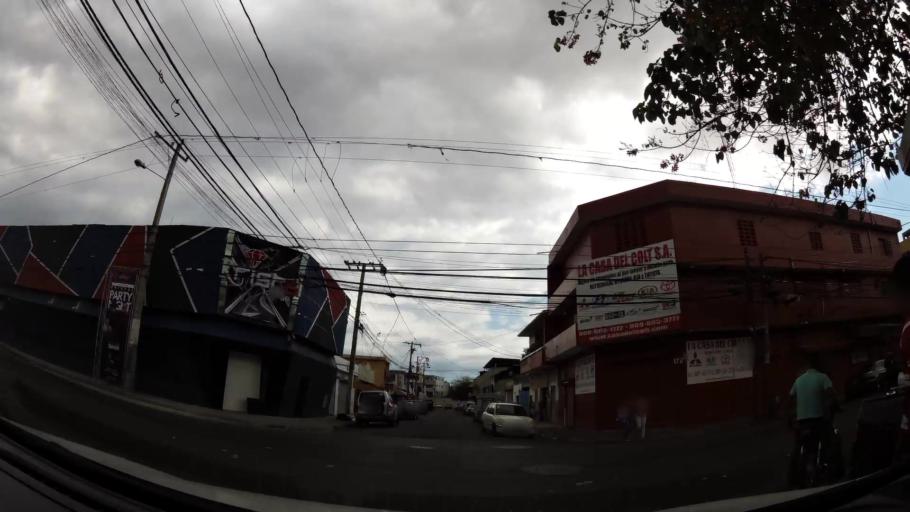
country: DO
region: Nacional
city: San Carlos
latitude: 18.4862
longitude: -69.9167
